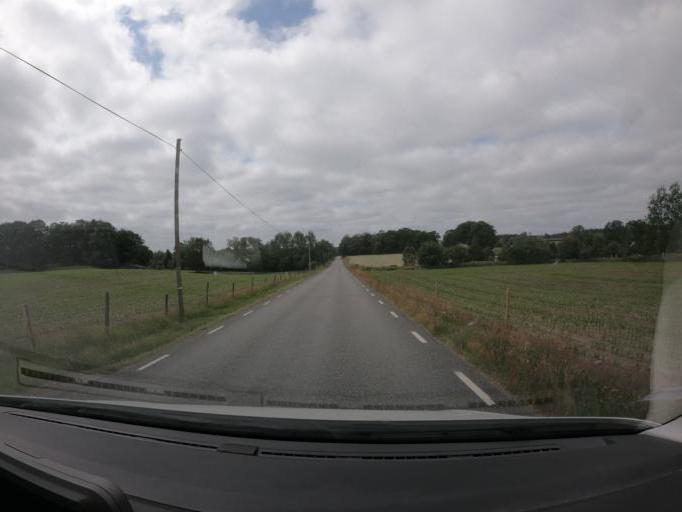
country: SE
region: Skane
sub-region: Hassleholms Kommun
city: Sosdala
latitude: 56.0652
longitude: 13.5538
